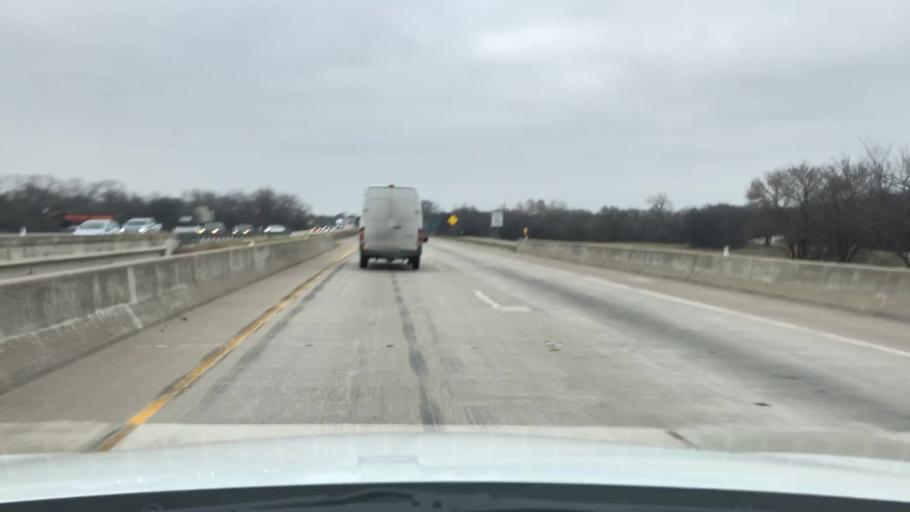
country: US
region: Texas
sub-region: Denton County
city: Sanger
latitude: 33.3331
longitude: -97.1809
